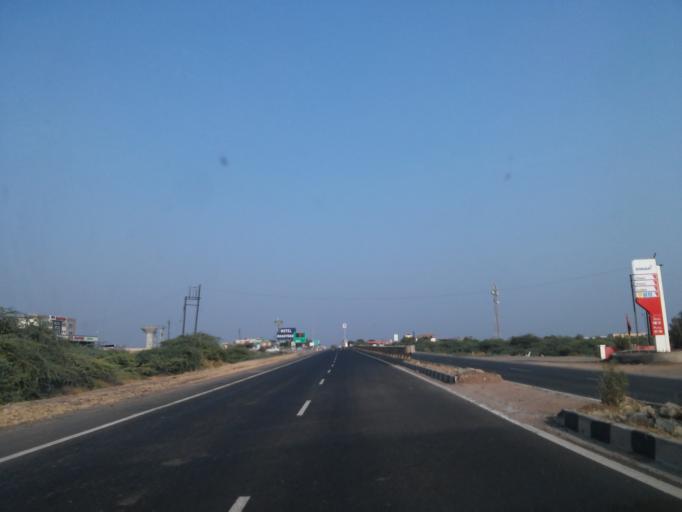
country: IN
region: Gujarat
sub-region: Surendranagar
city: Lakhtar
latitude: 23.0635
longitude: 71.7468
